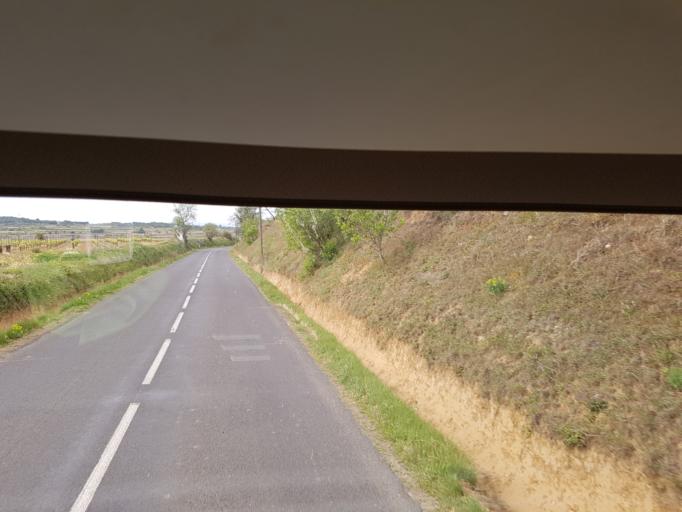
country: FR
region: Languedoc-Roussillon
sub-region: Departement de l'Aude
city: Fleury
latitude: 43.2126
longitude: 3.1356
